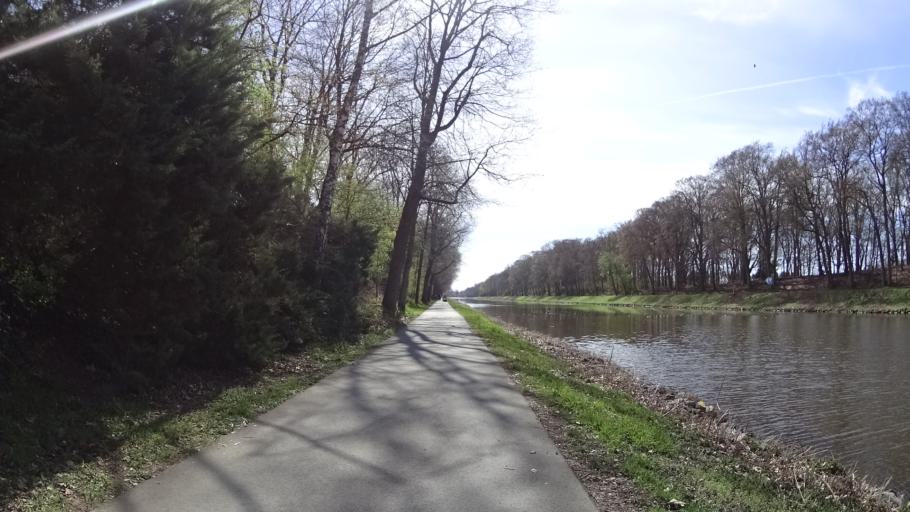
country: DE
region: Lower Saxony
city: Lingen
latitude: 52.5385
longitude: 7.2970
